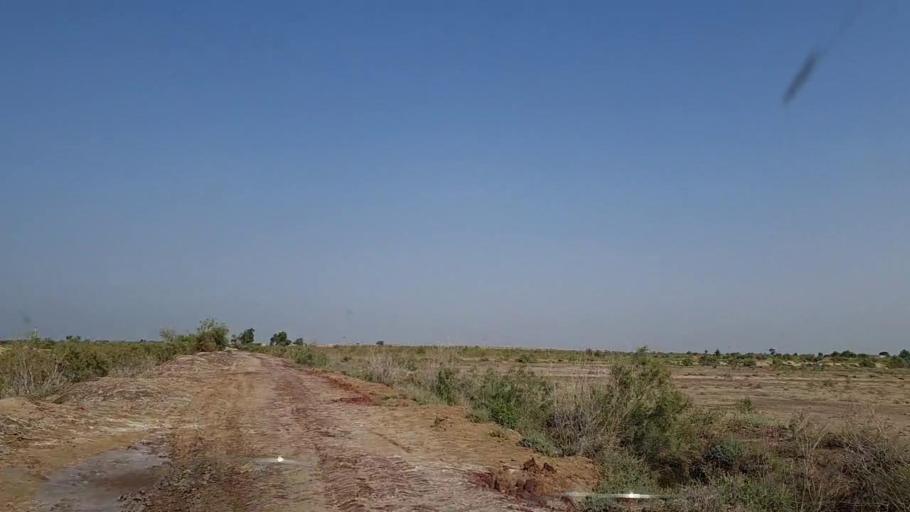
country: PK
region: Sindh
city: Khanpur
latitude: 27.6755
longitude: 69.3695
